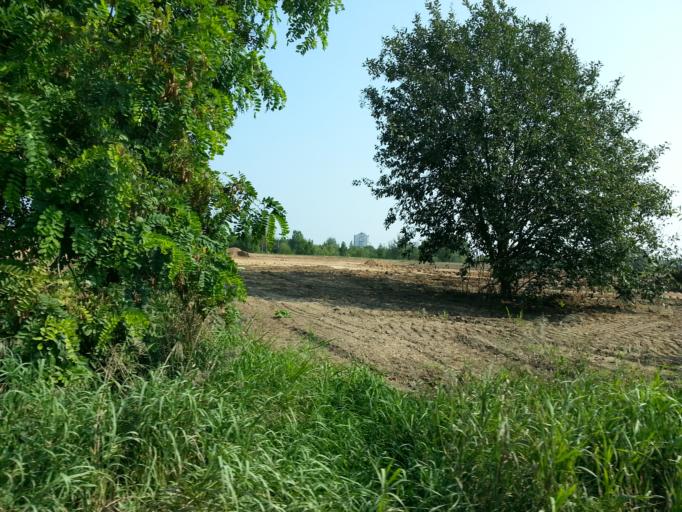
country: LT
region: Vilnius County
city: Pasilaiciai
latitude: 54.7281
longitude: 25.2060
